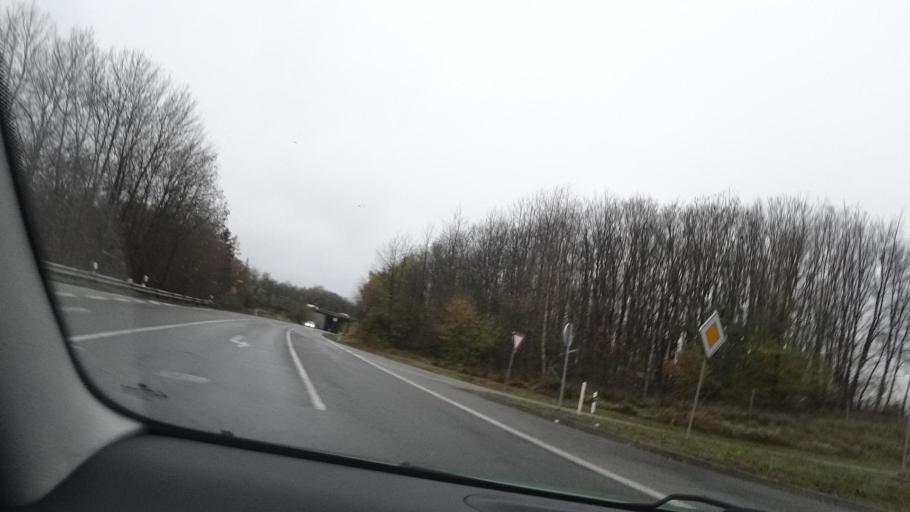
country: DE
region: Rheinland-Pfalz
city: Birkheim
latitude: 50.1194
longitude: 7.6035
